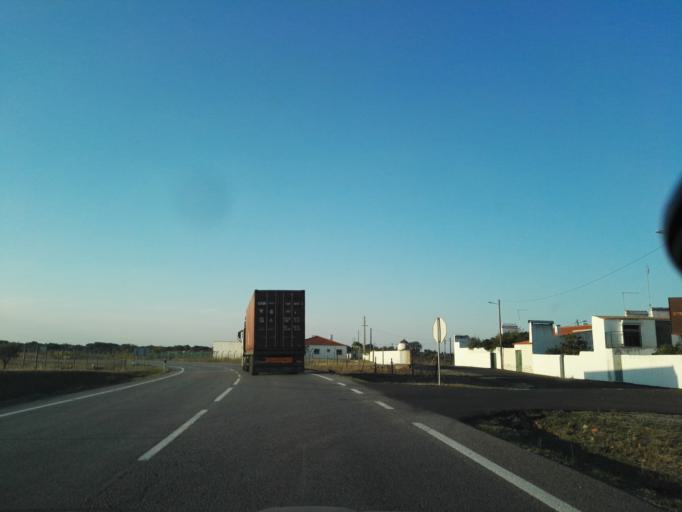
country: PT
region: Evora
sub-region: Arraiolos
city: Arraiolos
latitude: 38.8325
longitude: -7.8453
